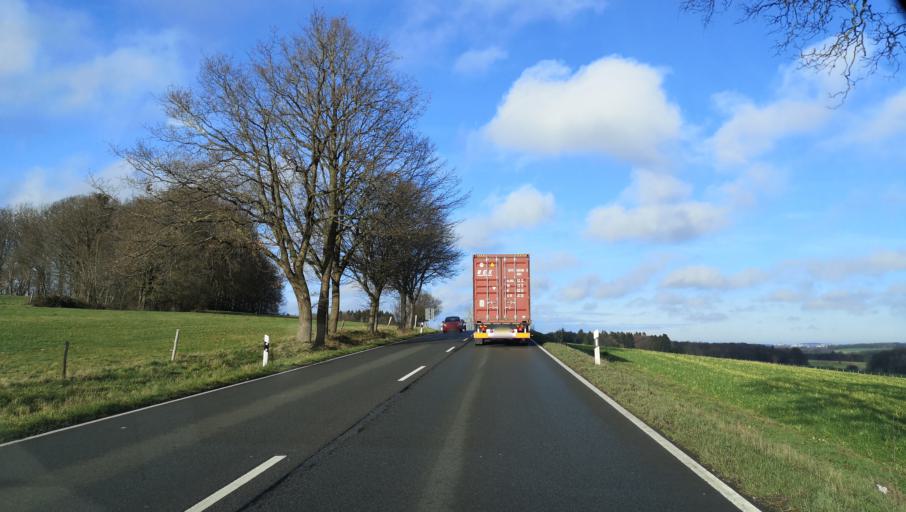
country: DE
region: North Rhine-Westphalia
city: Radevormwald
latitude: 51.2218
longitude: 7.3730
